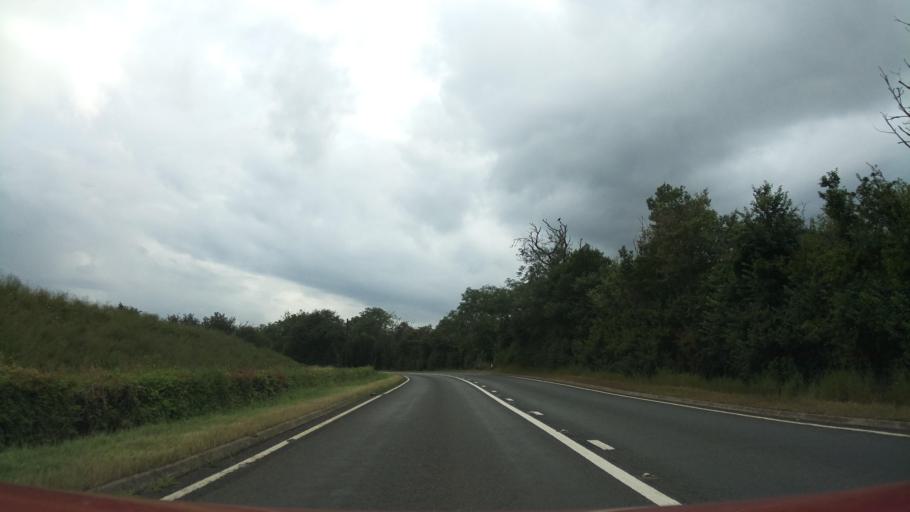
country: GB
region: England
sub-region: Warwickshire
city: Southam
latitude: 52.2658
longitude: -1.3809
